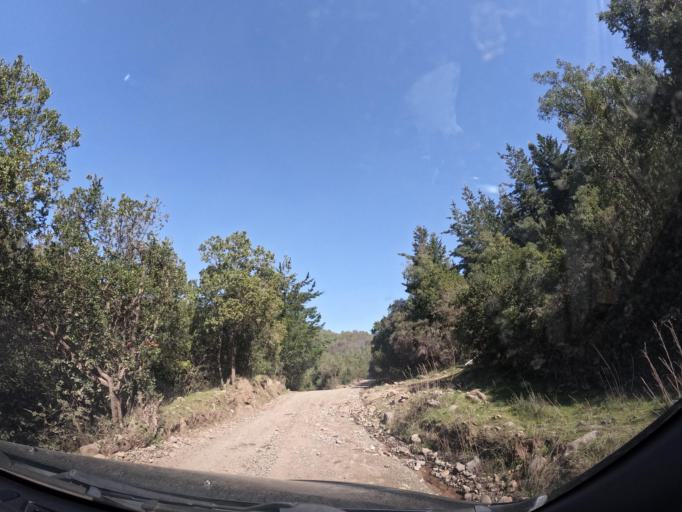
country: CL
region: Maule
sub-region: Provincia de Linares
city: Longavi
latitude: -36.2395
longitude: -71.4409
